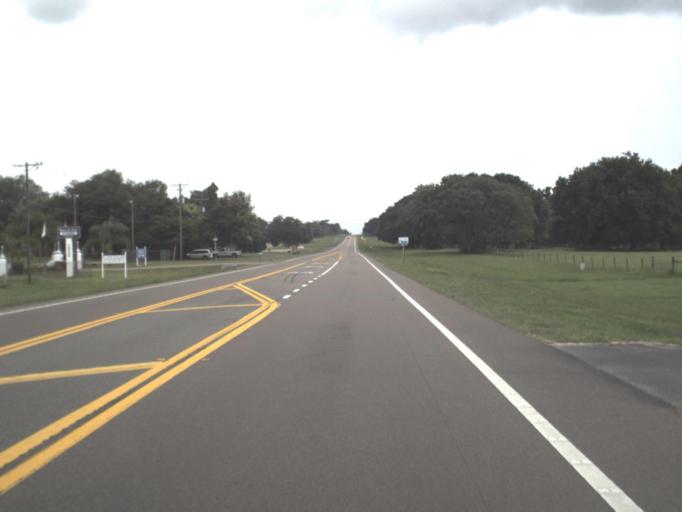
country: US
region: Florida
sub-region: Pasco County
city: Zephyrhills North
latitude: 28.3061
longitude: -82.1596
